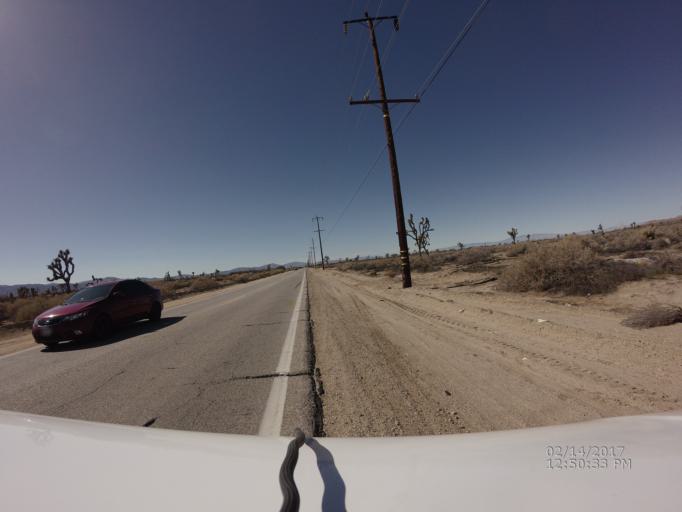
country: US
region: California
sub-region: Los Angeles County
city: Lake Los Angeles
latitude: 34.5801
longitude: -117.8855
